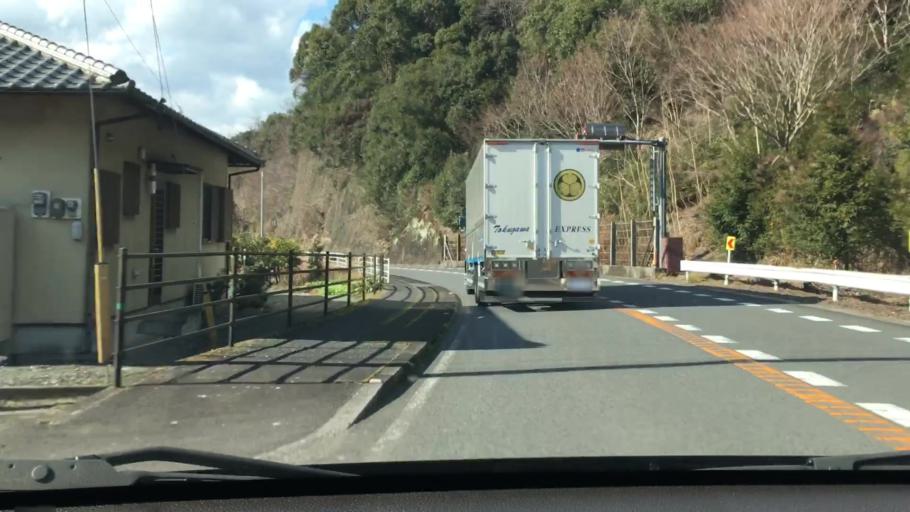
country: JP
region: Oita
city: Usuki
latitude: 32.9966
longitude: 131.7580
